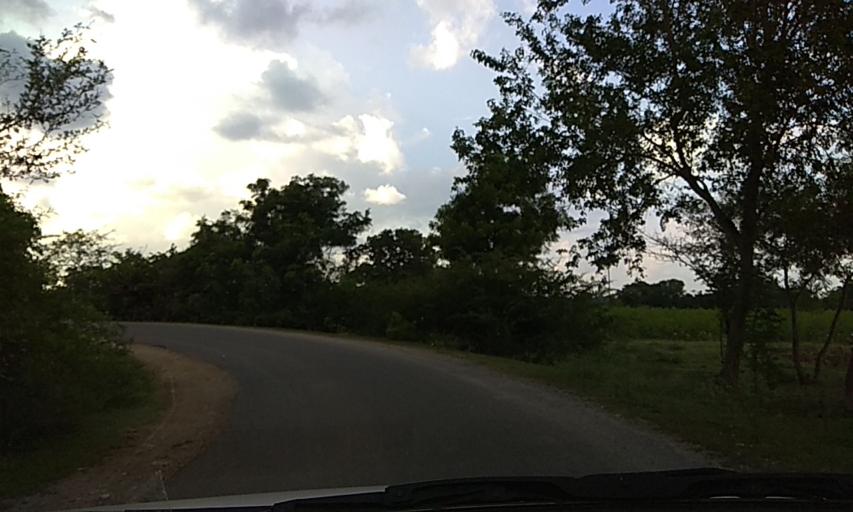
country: IN
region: Karnataka
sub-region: Chamrajnagar
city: Gundlupet
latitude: 11.8712
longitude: 76.7323
